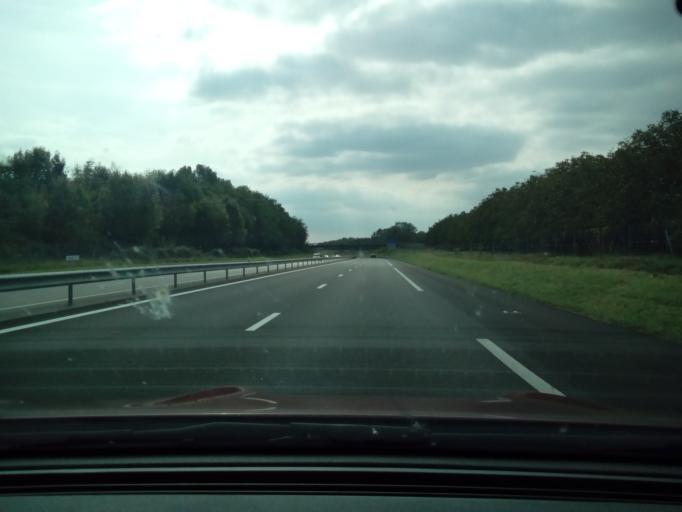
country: FR
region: Rhone-Alpes
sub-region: Departement de l'Isere
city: Vinay
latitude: 45.1865
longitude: 5.4082
